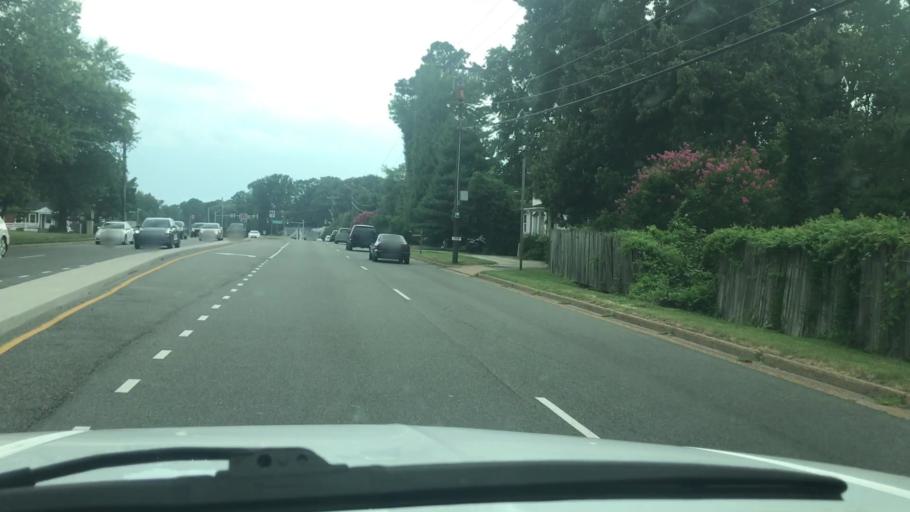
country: US
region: Virginia
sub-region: Henrico County
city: Tuckahoe
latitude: 37.6200
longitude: -77.5585
